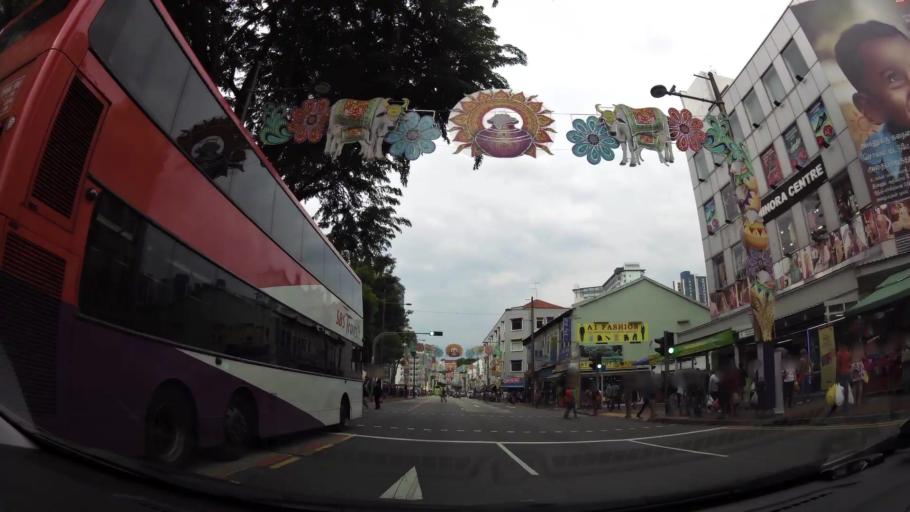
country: SG
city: Singapore
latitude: 1.3089
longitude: 103.8533
